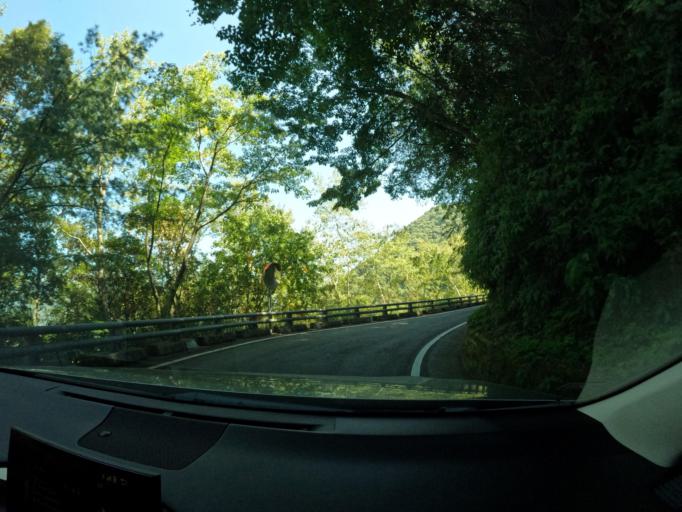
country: TW
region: Taiwan
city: Yujing
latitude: 23.2815
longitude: 120.9050
